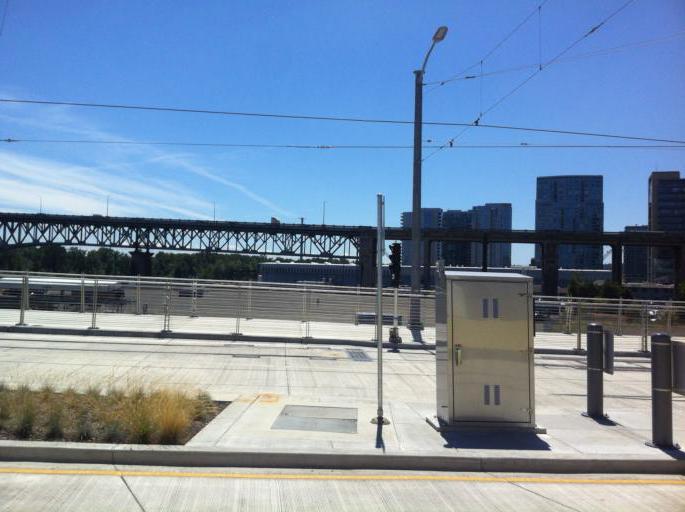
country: US
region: Oregon
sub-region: Multnomah County
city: Portland
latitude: 45.5030
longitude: -122.6701
